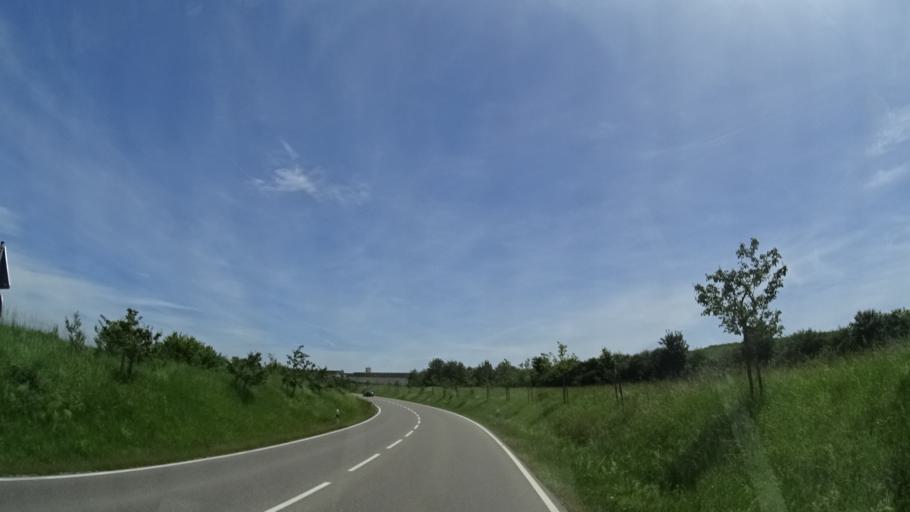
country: DE
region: Baden-Wuerttemberg
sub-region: Regierungsbezirk Stuttgart
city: Schwaebisch Hall
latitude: 49.1187
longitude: 9.7694
